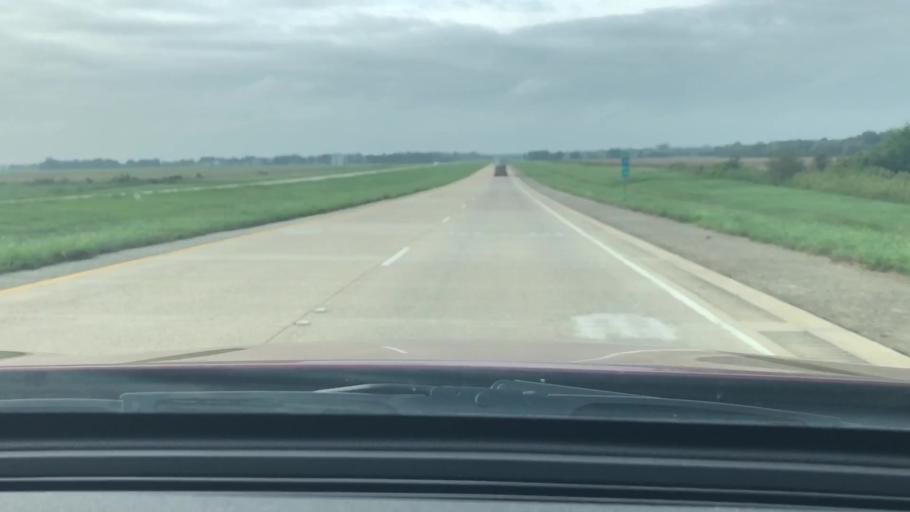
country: US
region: Louisiana
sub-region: Caddo Parish
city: Vivian
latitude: 32.8787
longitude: -93.8604
